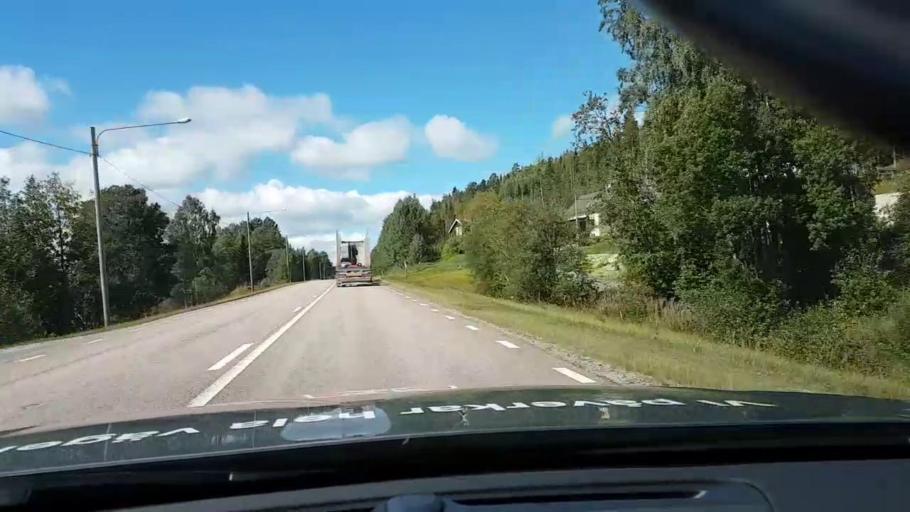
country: SE
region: Vaesternorrland
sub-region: OErnskoeldsviks Kommun
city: Bjasta
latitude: 63.3828
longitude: 18.4024
